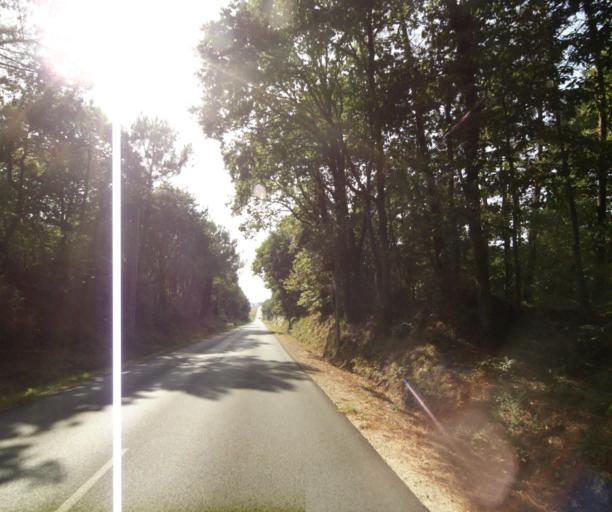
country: FR
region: Brittany
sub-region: Departement du Morbihan
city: Riantec
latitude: 47.7175
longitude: -3.2915
